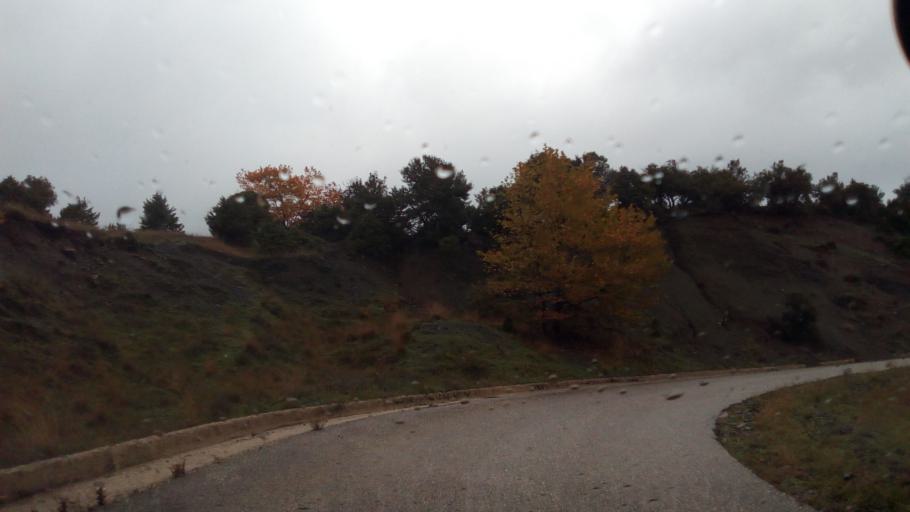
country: GR
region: West Greece
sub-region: Nomos Aitolias kai Akarnanias
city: Thermo
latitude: 38.6818
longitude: 21.8548
